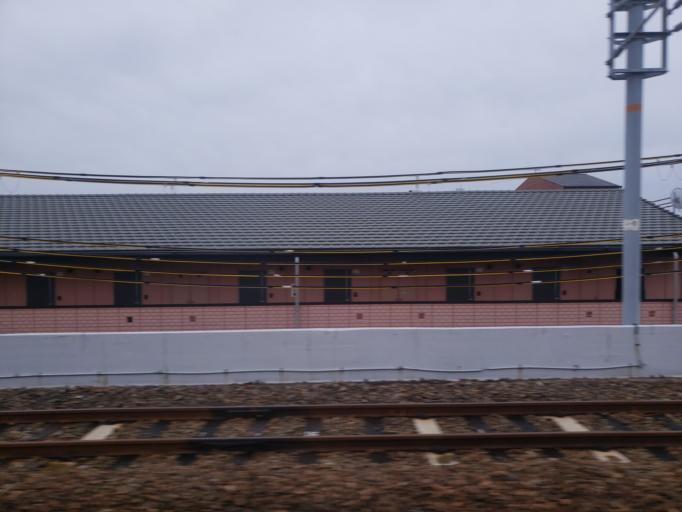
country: JP
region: Hyogo
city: Kobe
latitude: 34.6638
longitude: 135.1573
